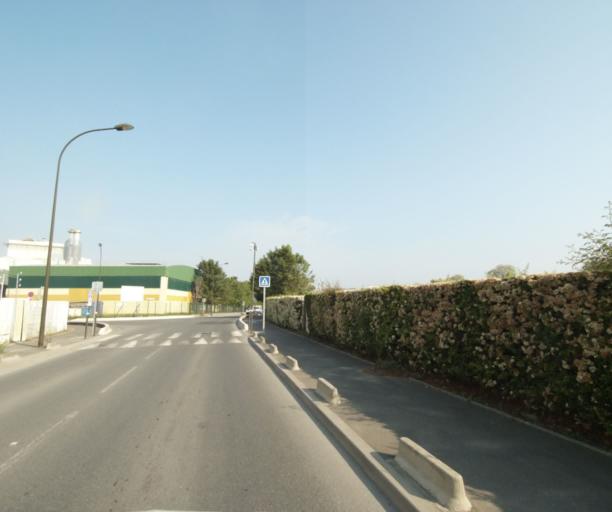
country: FR
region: Ile-de-France
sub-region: Departement du Val-d'Oise
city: Cormeilles-en-Parisis
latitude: 48.9574
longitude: 2.2095
